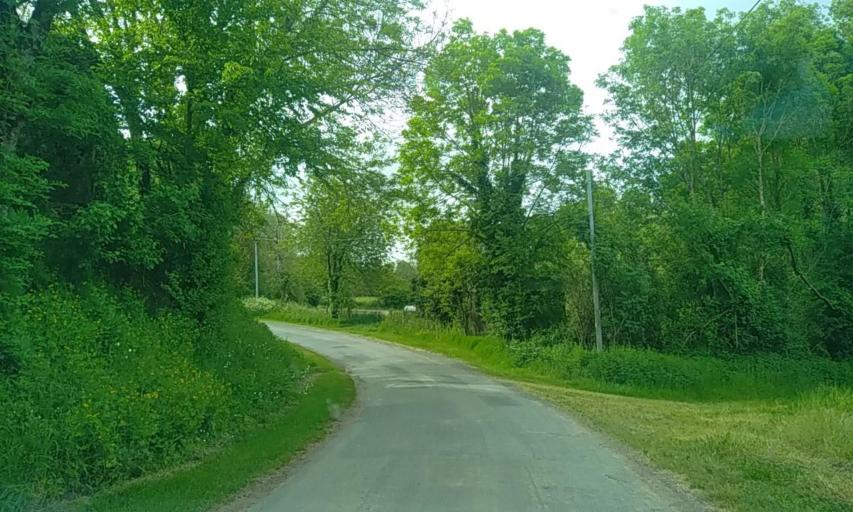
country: FR
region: Poitou-Charentes
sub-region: Departement des Deux-Sevres
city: Boisme
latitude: 46.7675
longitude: -0.4260
